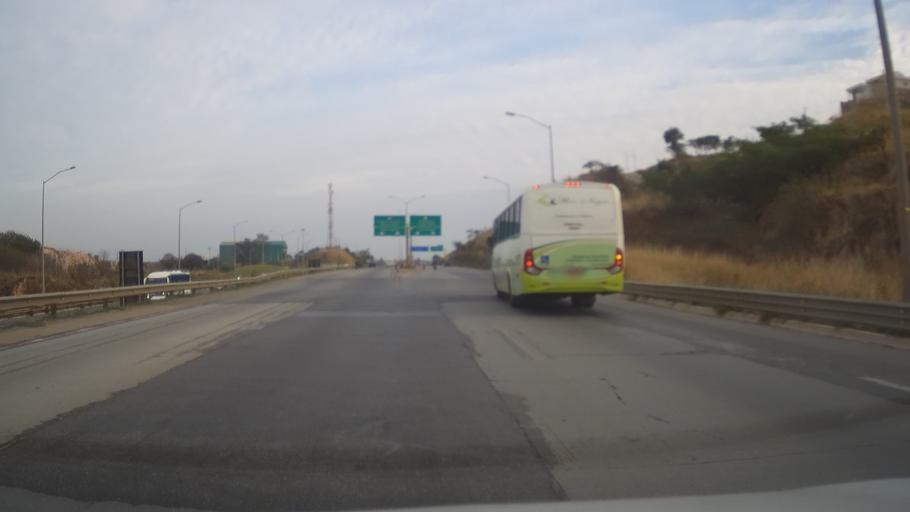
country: BR
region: Minas Gerais
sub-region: Vespasiano
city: Vespasiano
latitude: -19.7643
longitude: -43.9481
